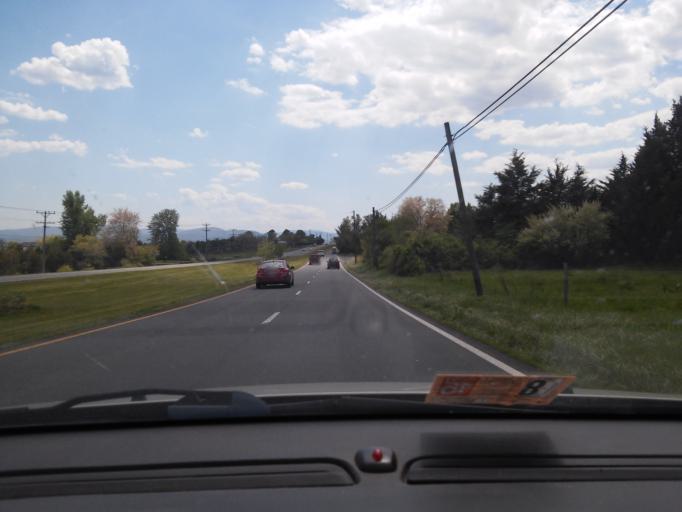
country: US
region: Virginia
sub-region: Warren County
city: Front Royal
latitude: 39.0054
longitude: -78.1704
